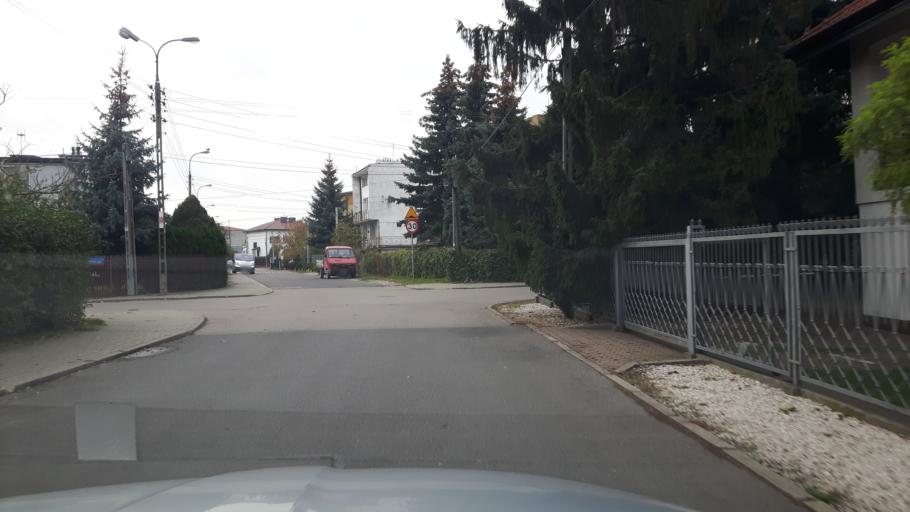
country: PL
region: Masovian Voivodeship
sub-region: Warszawa
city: Targowek
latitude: 52.2884
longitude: 21.0674
